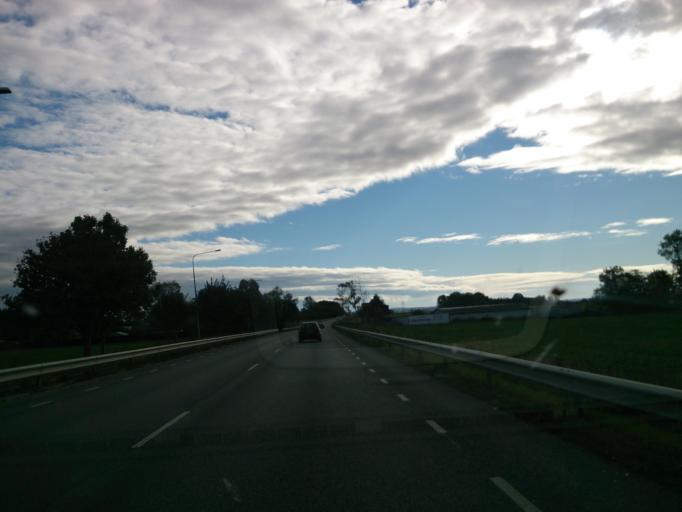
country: SE
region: Skane
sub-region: Staffanstorps Kommun
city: Staffanstorp
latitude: 55.6854
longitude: 13.2653
